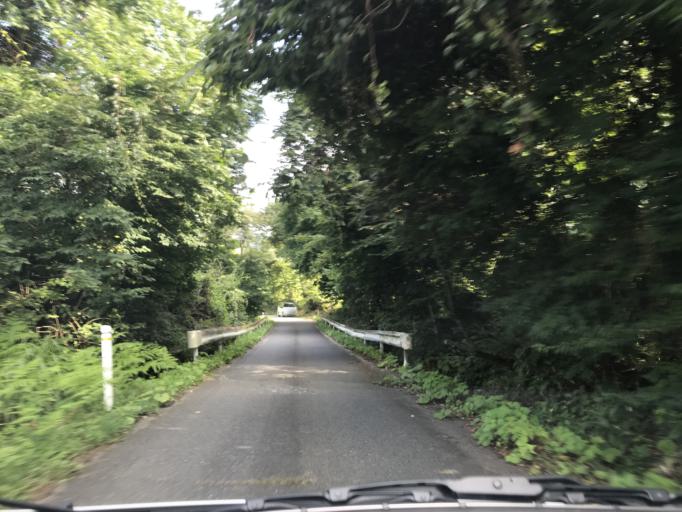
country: JP
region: Iwate
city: Ofunato
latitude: 38.9767
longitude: 141.4689
